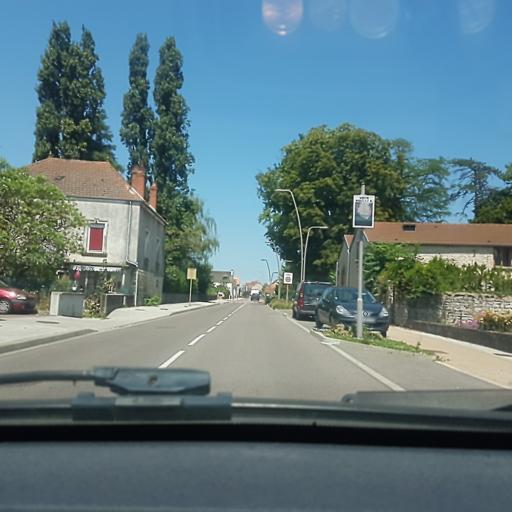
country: FR
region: Bourgogne
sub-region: Departement de Saone-et-Loire
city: Saint-Marcel
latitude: 46.7666
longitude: 4.8933
